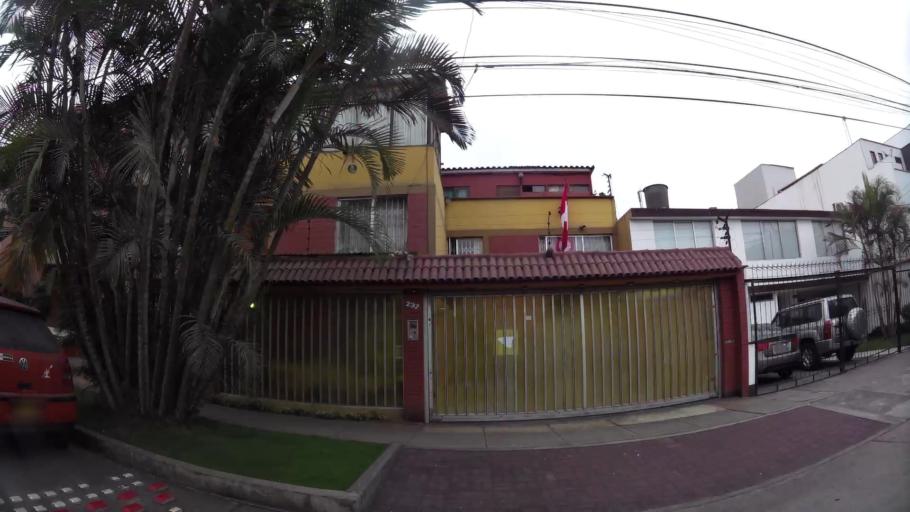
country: PE
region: Lima
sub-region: Lima
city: Surco
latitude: -12.1200
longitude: -76.9905
